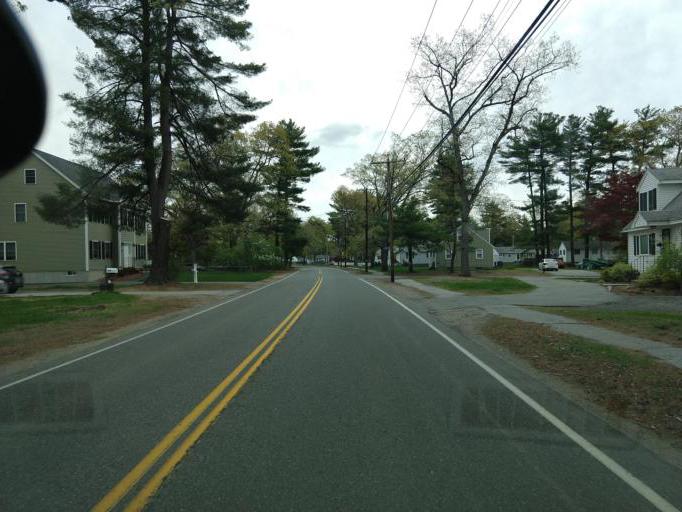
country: US
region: Massachusetts
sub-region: Middlesex County
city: Tewksbury
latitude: 42.5846
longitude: -71.2117
